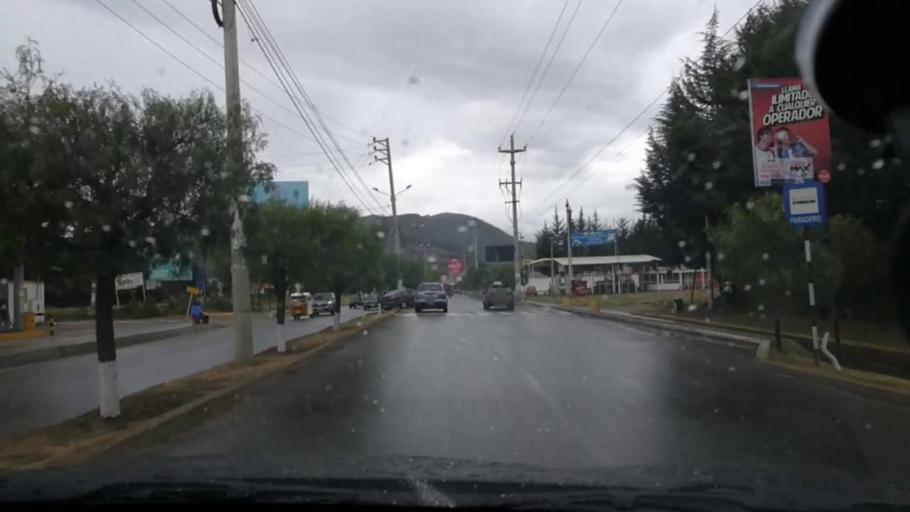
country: PE
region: Cajamarca
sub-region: Provincia de Cajamarca
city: Cajamarca
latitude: -7.1649
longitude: -78.4751
